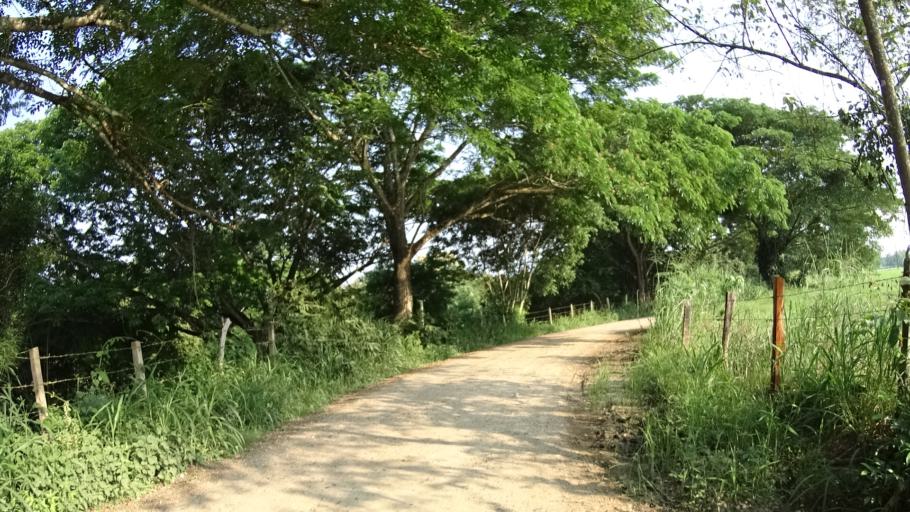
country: CO
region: Cundinamarca
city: Puerto Salgar
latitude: 5.5331
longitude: -74.6845
